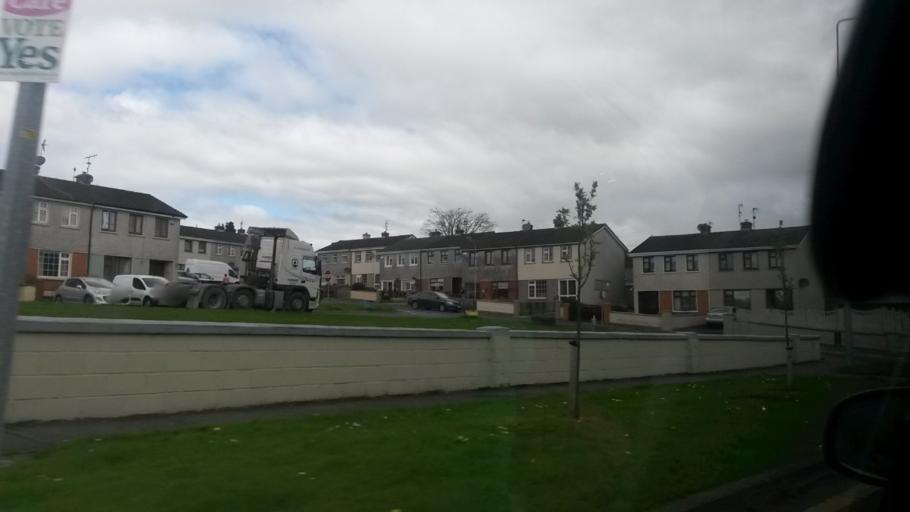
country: IE
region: Munster
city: Cashel
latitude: 52.5100
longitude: -7.8913
